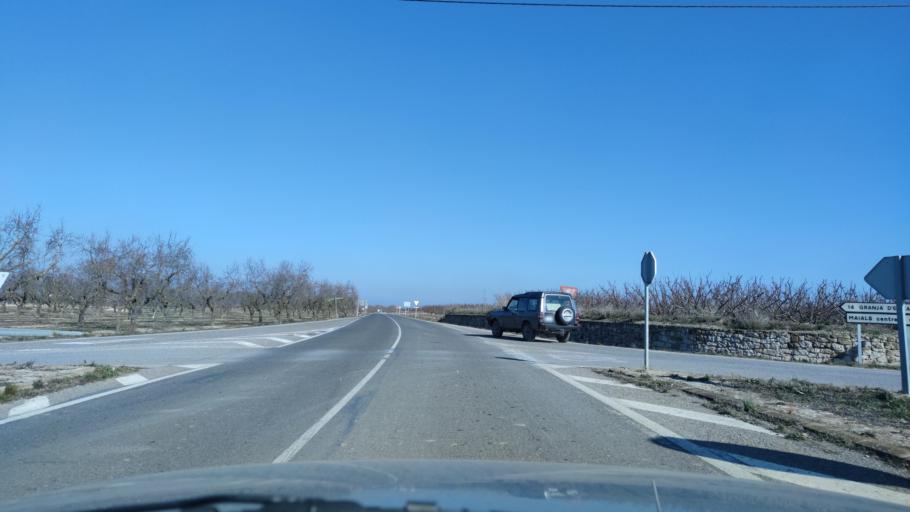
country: ES
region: Catalonia
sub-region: Provincia de Lleida
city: Maials
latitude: 41.3656
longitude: 0.4945
